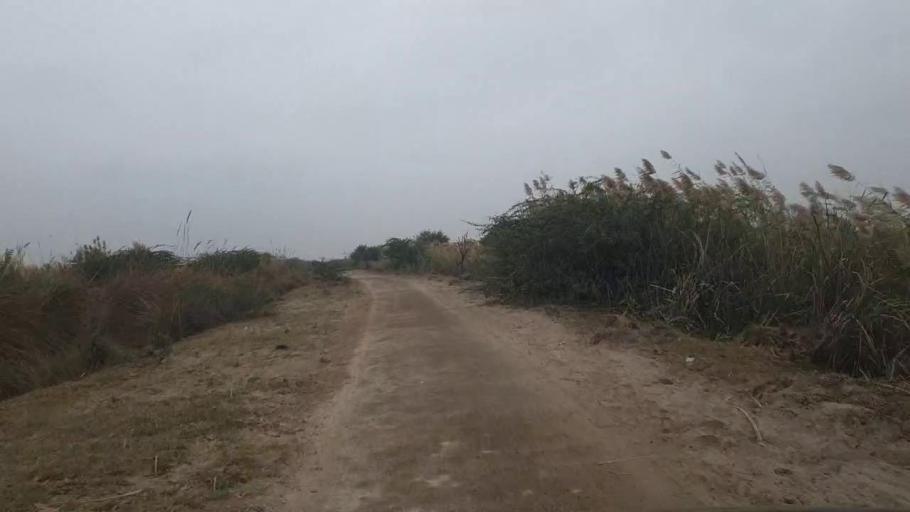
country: PK
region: Sindh
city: Tando Adam
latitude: 25.8371
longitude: 68.7217
